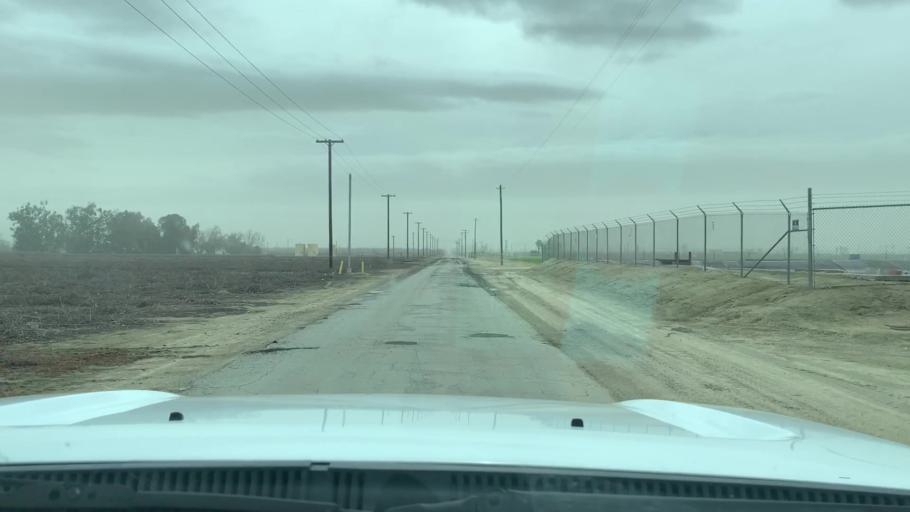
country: US
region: California
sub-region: Kern County
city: Shafter
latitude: 35.5353
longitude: -119.2689
